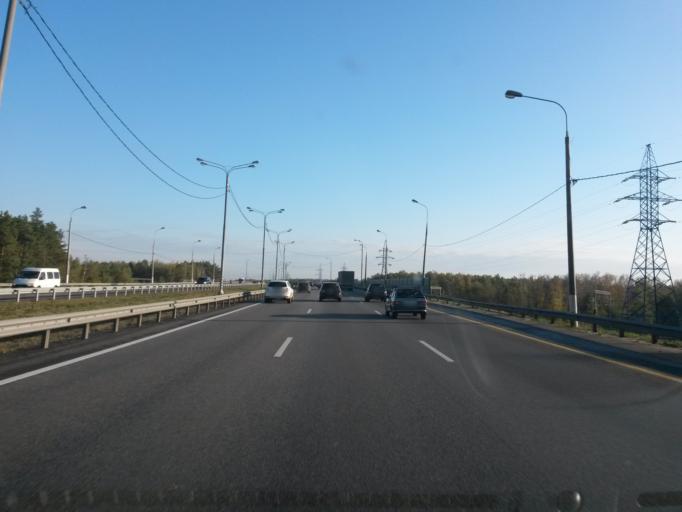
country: RU
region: Moskovskaya
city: Vostryakovo
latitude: 55.4107
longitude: 37.7912
